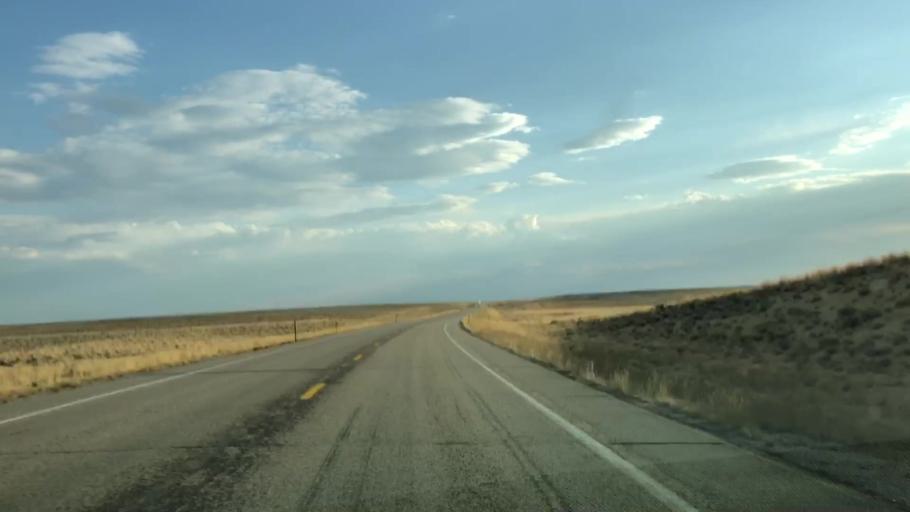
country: US
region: Wyoming
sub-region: Sweetwater County
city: North Rock Springs
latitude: 42.2155
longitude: -109.4703
